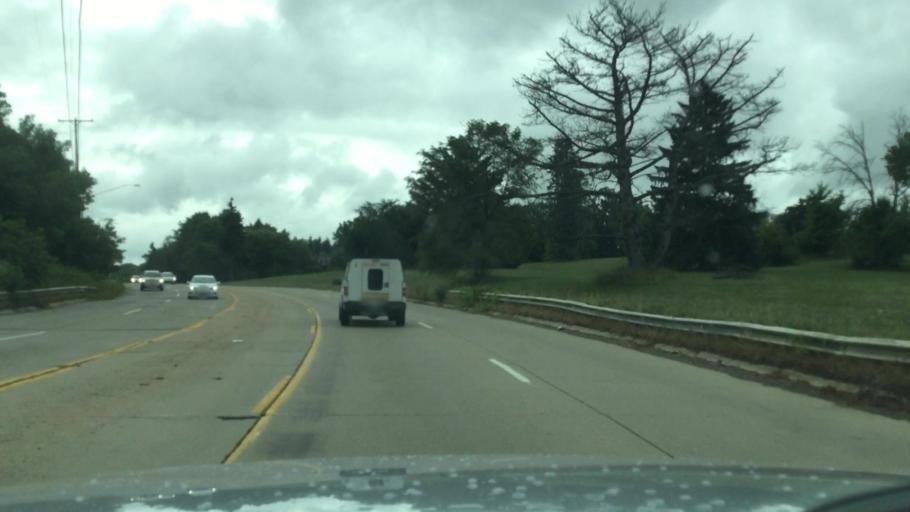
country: US
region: Michigan
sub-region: Genesee County
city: Flushing
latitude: 43.0443
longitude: -83.7737
